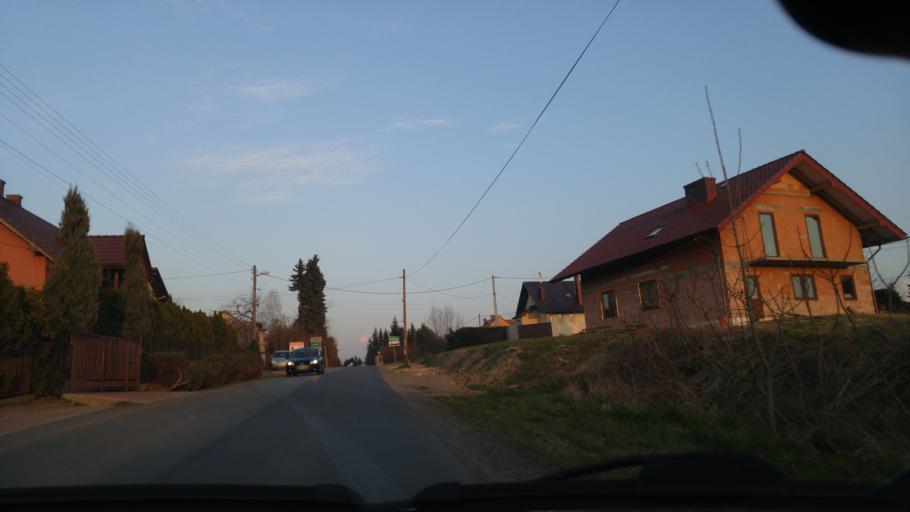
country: PL
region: Lesser Poland Voivodeship
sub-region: Powiat krakowski
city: Skawina
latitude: 49.9456
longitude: 19.8515
